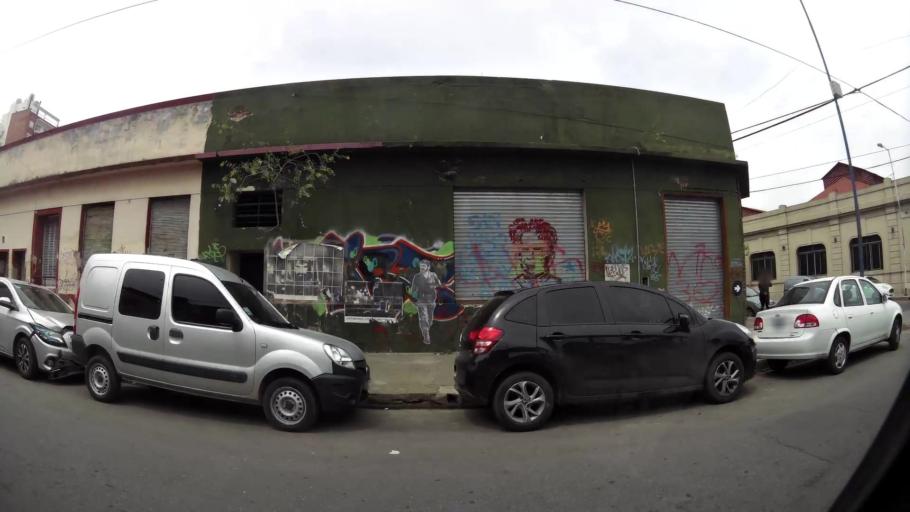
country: AR
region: Buenos Aires
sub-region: Partido de Avellaneda
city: Avellaneda
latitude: -34.6626
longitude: -58.3716
